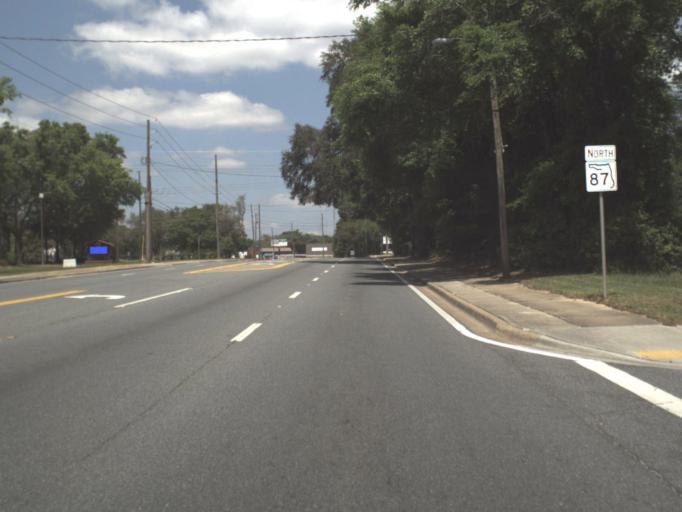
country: US
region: Florida
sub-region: Santa Rosa County
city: Milton
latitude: 30.6388
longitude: -87.0430
